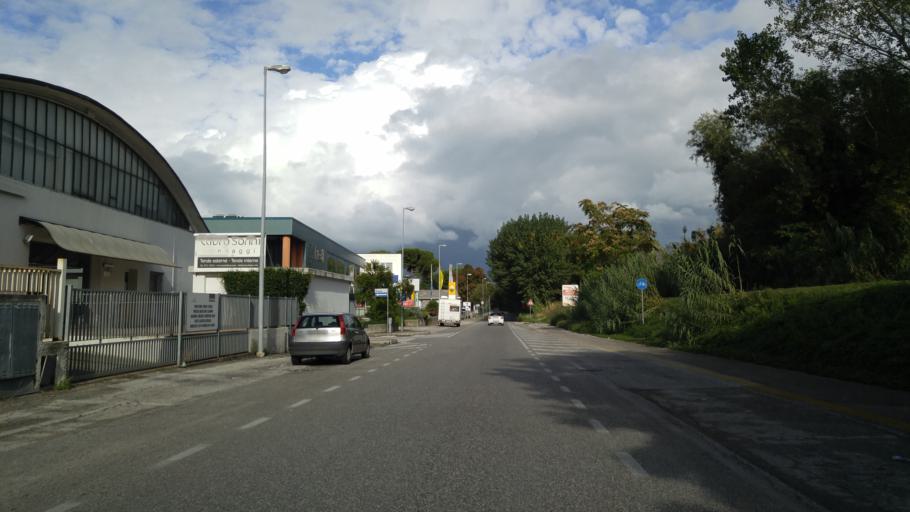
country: IT
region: The Marches
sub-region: Provincia di Pesaro e Urbino
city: Pesaro
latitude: 43.9058
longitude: 12.8936
